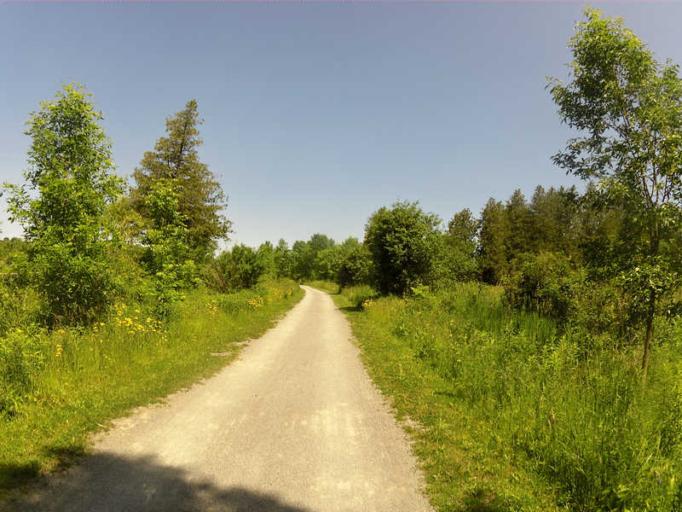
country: CA
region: Ontario
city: Peterborough
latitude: 44.4139
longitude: -78.2629
